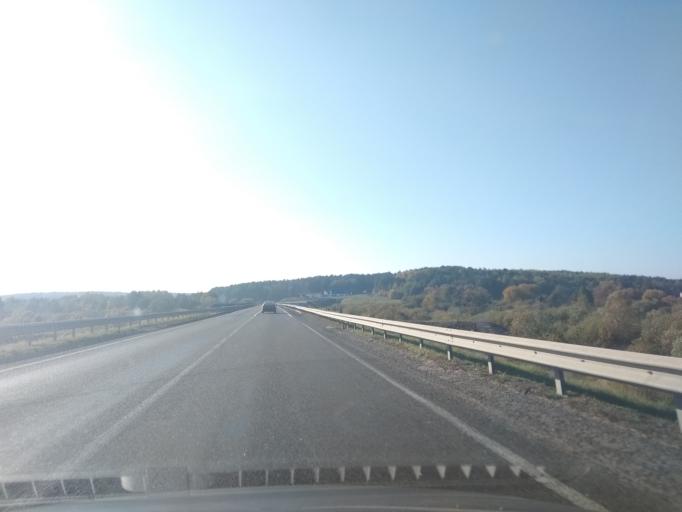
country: BY
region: Grodnenskaya
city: Zhyrovichy
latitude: 53.0478
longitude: 25.3671
